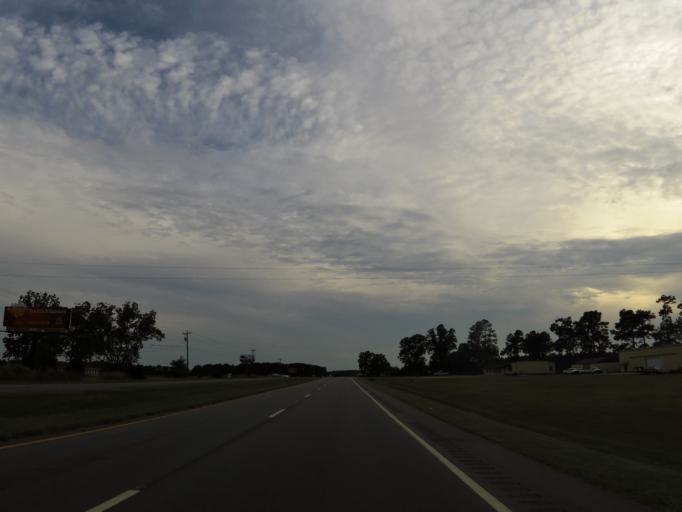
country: US
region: Alabama
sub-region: Escambia County
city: Atmore
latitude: 31.0707
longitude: -87.4869
